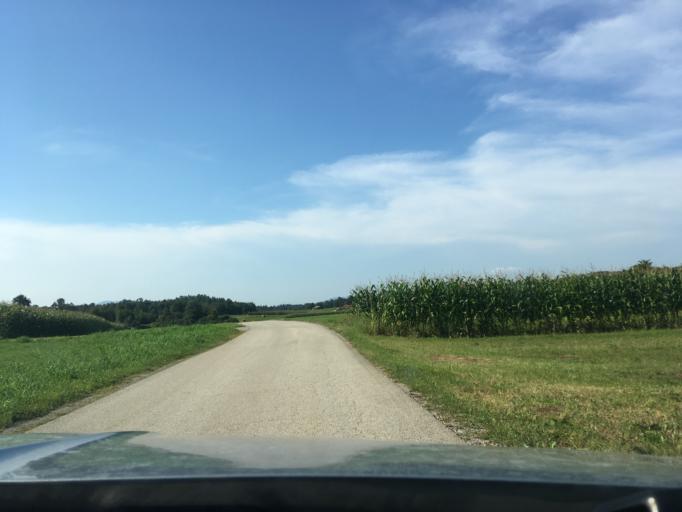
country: SI
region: Crnomelj
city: Crnomelj
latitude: 45.4717
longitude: 15.2090
